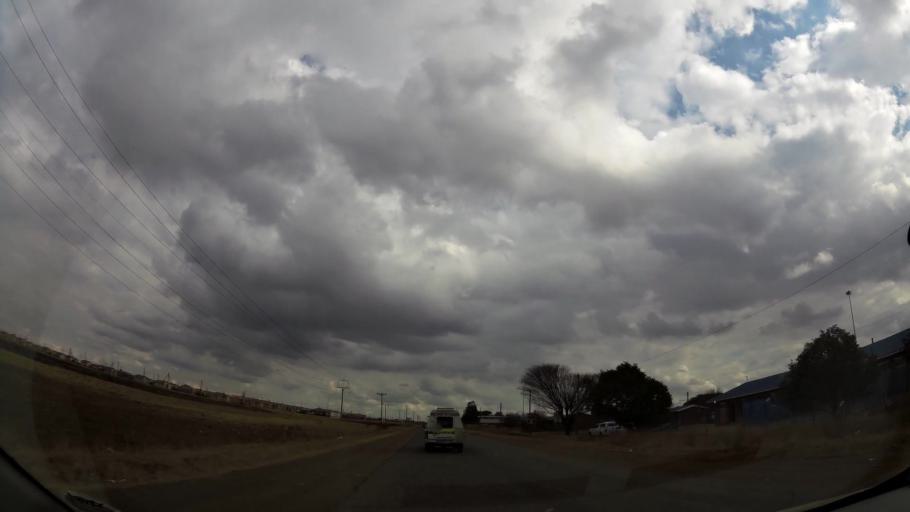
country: ZA
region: Orange Free State
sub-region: Fezile Dabi District Municipality
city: Sasolburg
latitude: -26.8551
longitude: 27.8668
